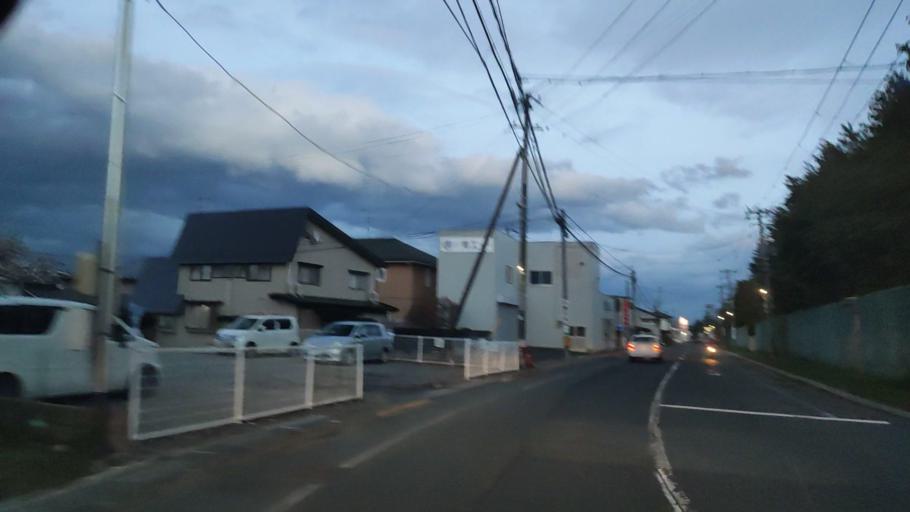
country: JP
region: Iwate
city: Morioka-shi
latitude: 39.7193
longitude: 141.1216
